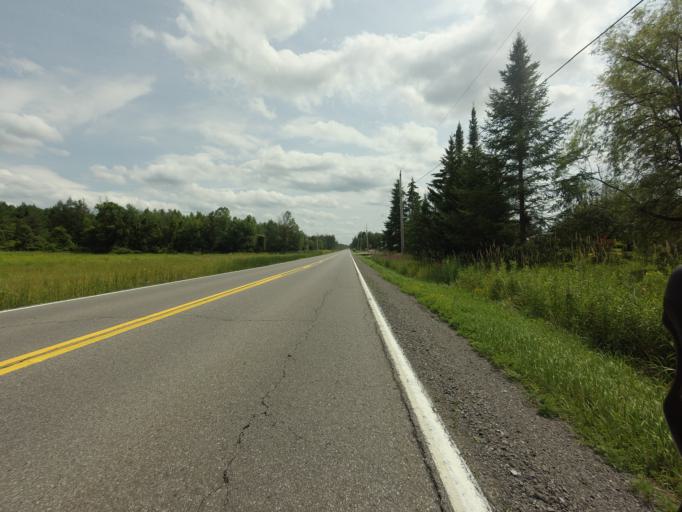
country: CA
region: Ontario
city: Ottawa
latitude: 45.2248
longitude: -75.6055
